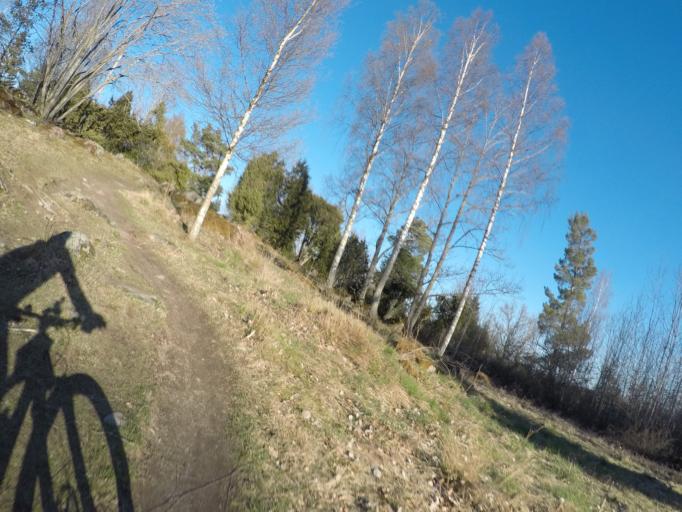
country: SE
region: Soedermanland
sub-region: Eskilstuna Kommun
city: Torshalla
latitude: 59.4096
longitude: 16.5054
